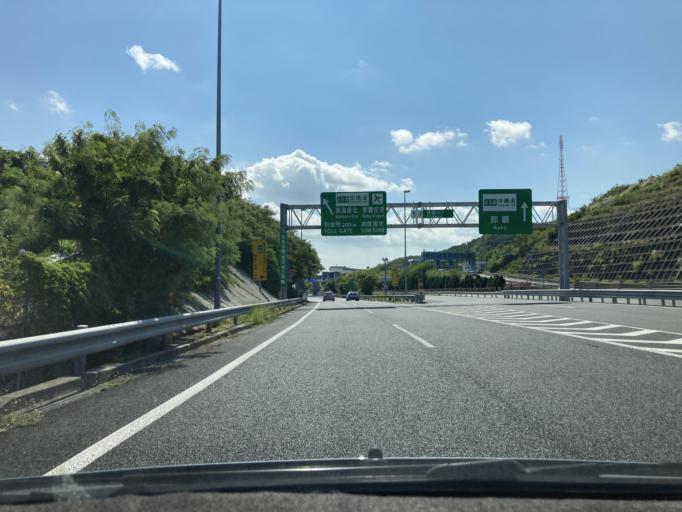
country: JP
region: Okinawa
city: Ginowan
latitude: 26.2235
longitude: 127.7383
